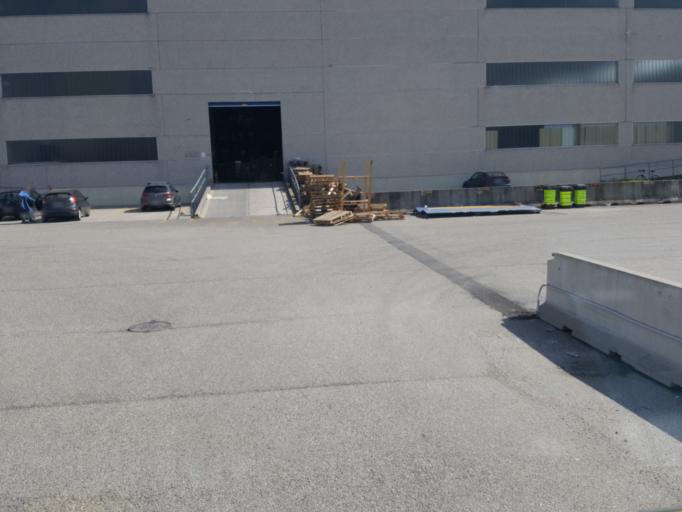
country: IT
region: Piedmont
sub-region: Provincia di Novara
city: Pernate
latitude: 45.4626
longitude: 8.6528
